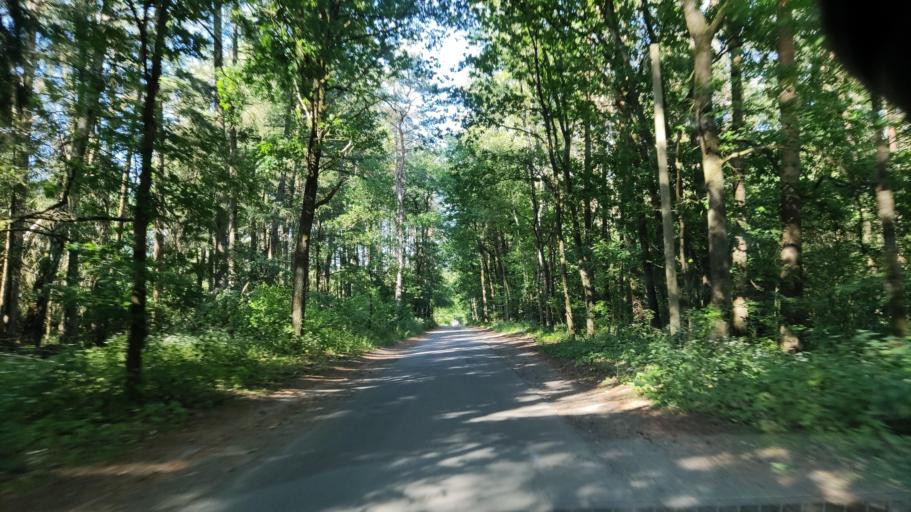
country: DE
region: Lower Saxony
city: Stelle
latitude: 53.3783
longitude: 10.0545
